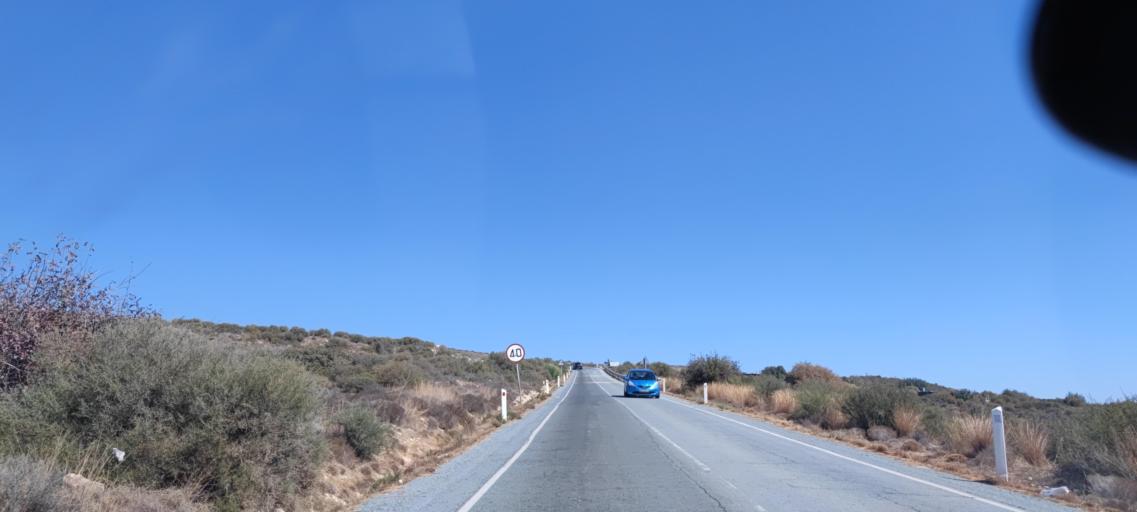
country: CY
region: Limassol
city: Mouttagiaka
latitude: 34.7414
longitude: 33.0628
